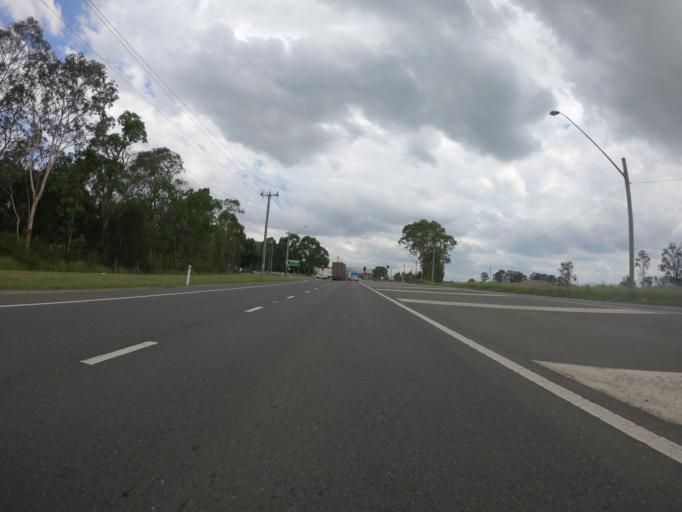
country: AU
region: New South Wales
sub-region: Blacktown
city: Mount Druitt
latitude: -33.8166
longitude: 150.7760
